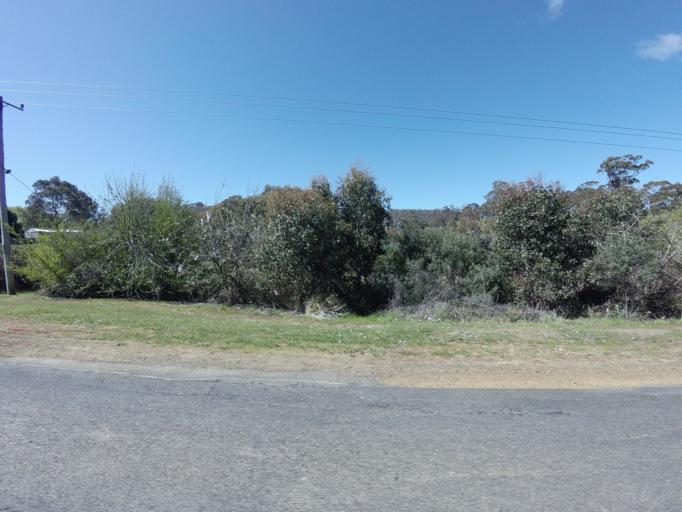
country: AU
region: Tasmania
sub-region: Derwent Valley
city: New Norfolk
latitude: -42.6230
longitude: 146.7212
